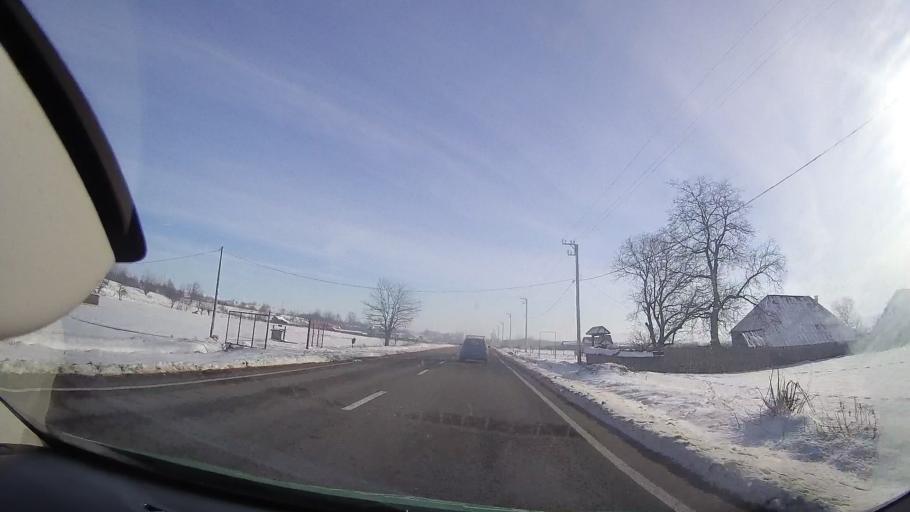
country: RO
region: Neamt
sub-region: Comuna Ghindaoani
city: Ghindaoani
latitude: 47.0794
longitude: 26.3471
